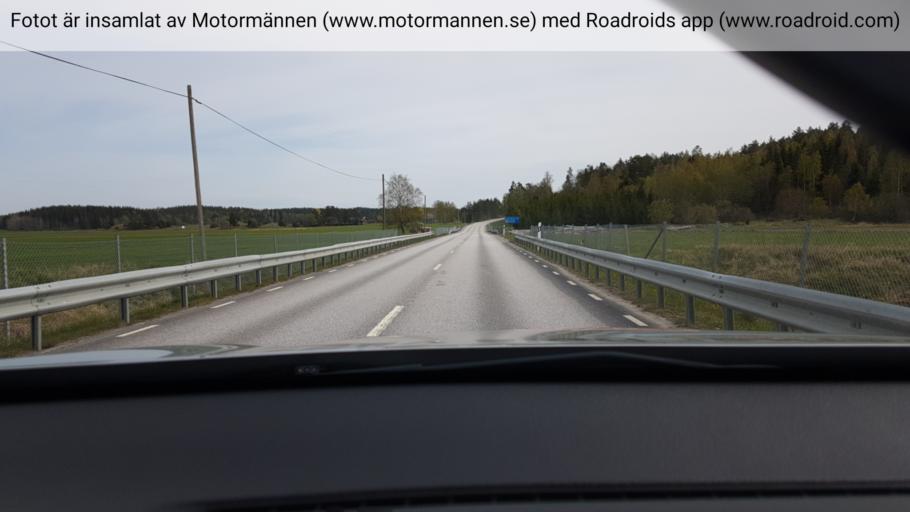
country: SE
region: Stockholm
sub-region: Vallentuna Kommun
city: Vallentuna
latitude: 59.7446
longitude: 18.0504
